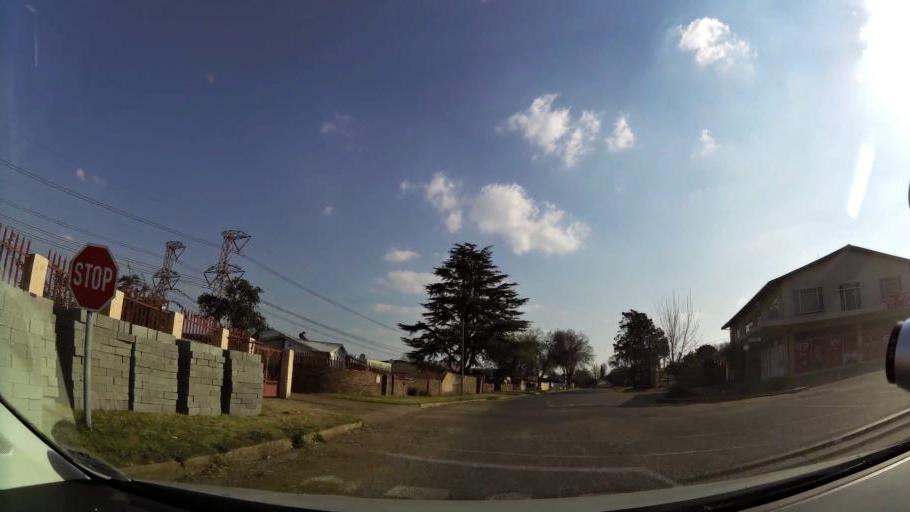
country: ZA
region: Gauteng
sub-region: City of Johannesburg Metropolitan Municipality
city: Modderfontein
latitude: -26.0875
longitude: 28.1943
